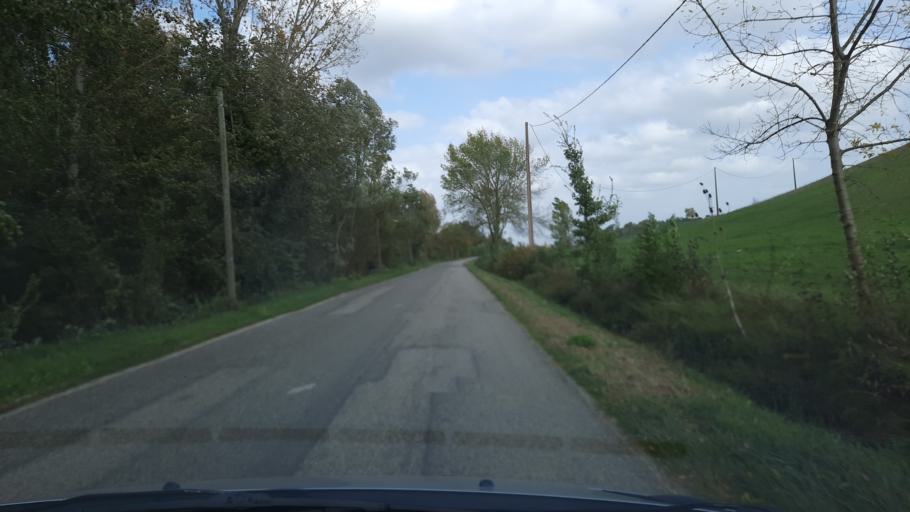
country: FR
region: Midi-Pyrenees
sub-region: Departement du Tarn-et-Garonne
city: Lafrancaise
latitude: 44.1786
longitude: 1.2769
